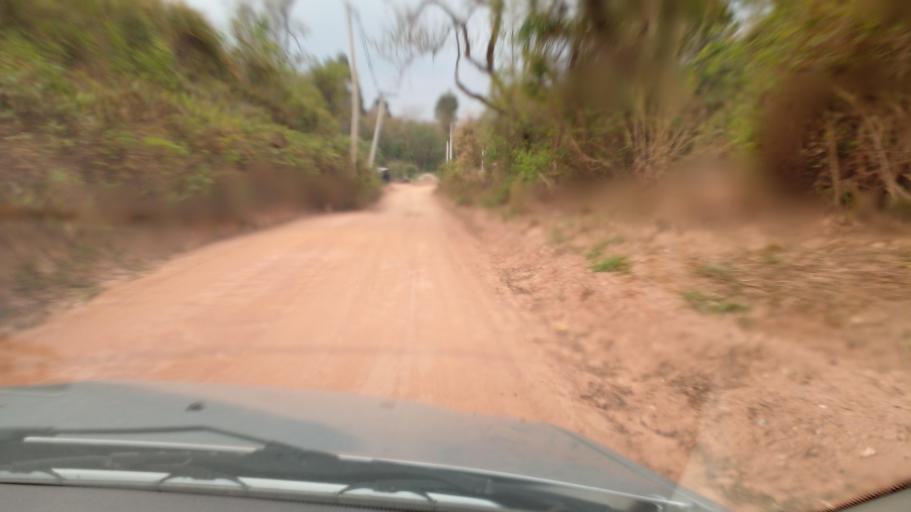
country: BR
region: Sao Paulo
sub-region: Louveira
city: Louveira
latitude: -23.1238
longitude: -46.9053
